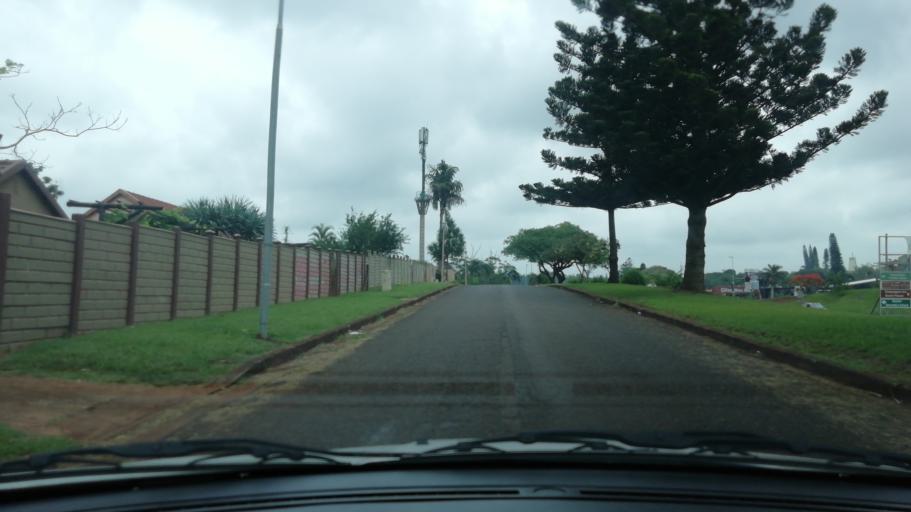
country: ZA
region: KwaZulu-Natal
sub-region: uThungulu District Municipality
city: Empangeni
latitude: -28.7603
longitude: 31.9026
